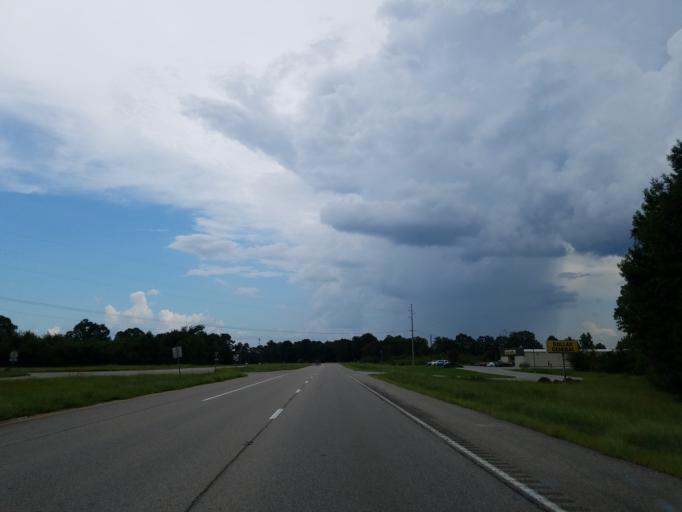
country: US
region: Mississippi
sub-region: Forrest County
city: Glendale
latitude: 31.3740
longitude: -89.3179
